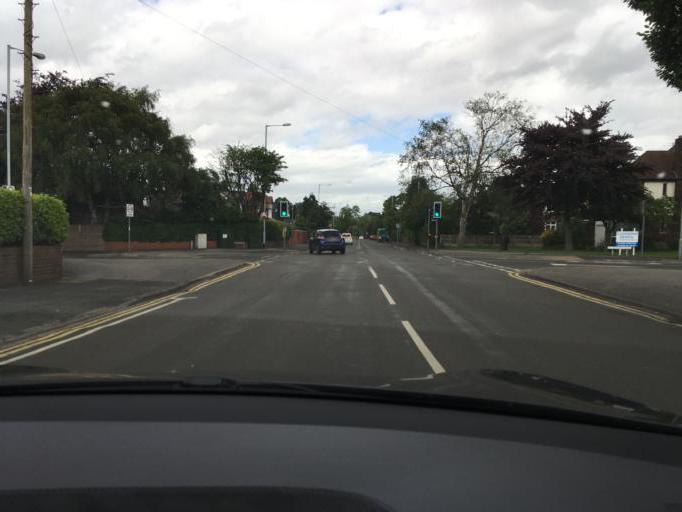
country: GB
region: England
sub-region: Borough of Stockport
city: Hazel Grove
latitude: 53.3717
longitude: -2.1240
